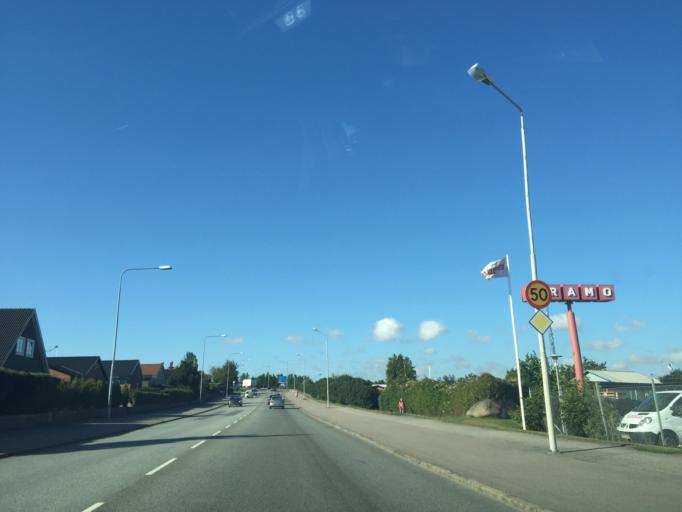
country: SE
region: Skane
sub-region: Ystads Kommun
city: Ystad
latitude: 55.4401
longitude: 13.8354
